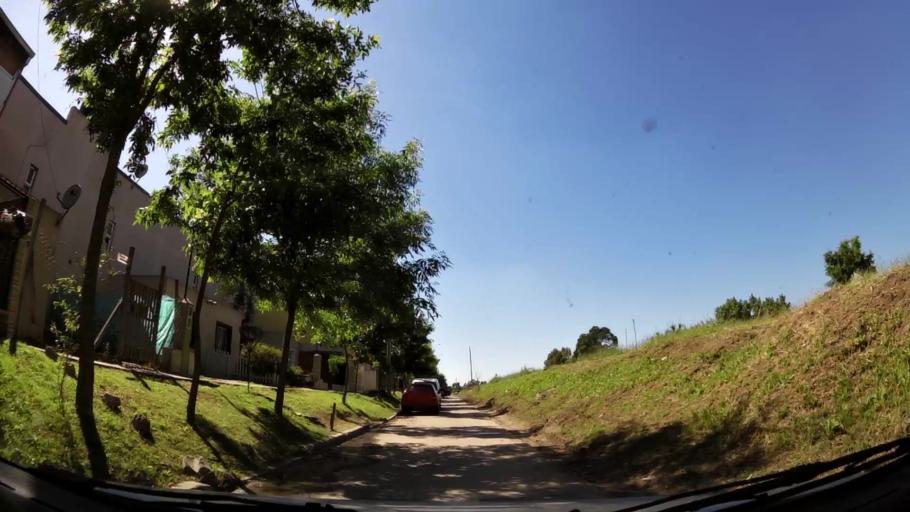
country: AR
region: Buenos Aires
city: Hurlingham
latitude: -34.6194
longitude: -58.6538
